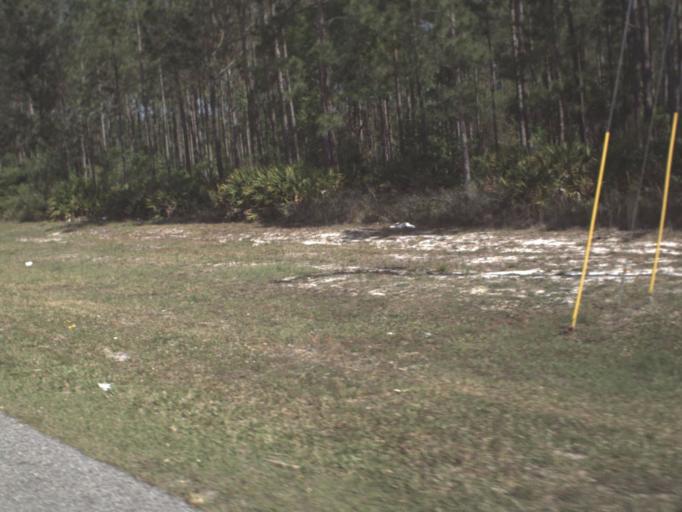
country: US
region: Florida
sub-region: Flagler County
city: Bunnell
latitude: 29.4320
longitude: -81.2305
